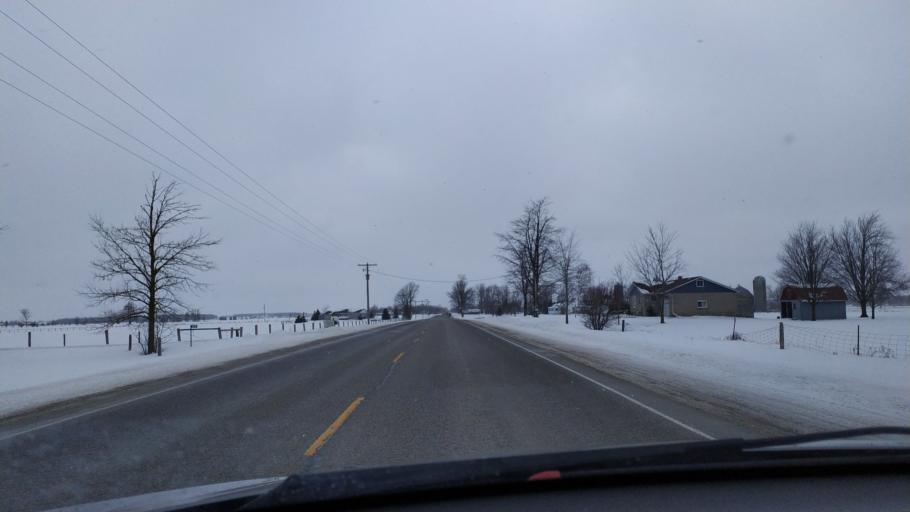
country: CA
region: Ontario
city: North Perth
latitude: 43.5797
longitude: -80.8540
